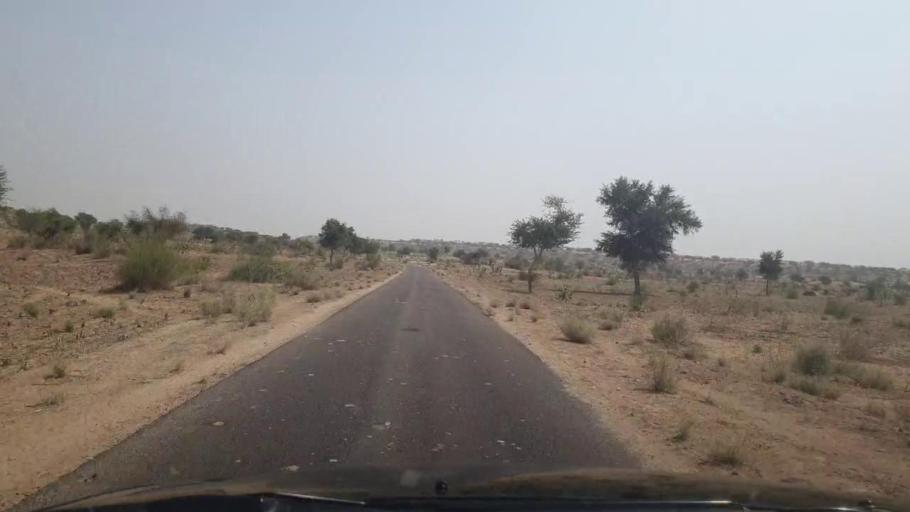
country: PK
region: Sindh
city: Islamkot
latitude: 24.9450
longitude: 70.4038
